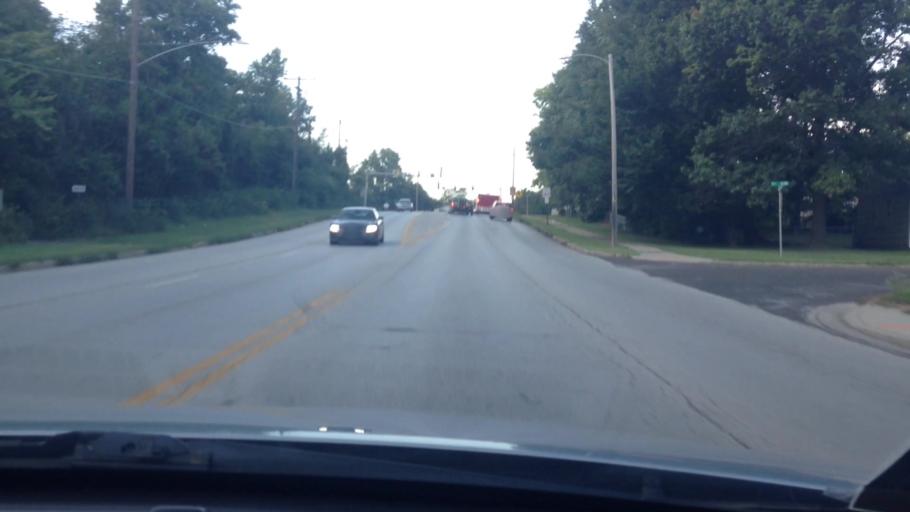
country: US
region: Missouri
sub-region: Jackson County
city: Raytown
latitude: 38.9938
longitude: -94.4820
